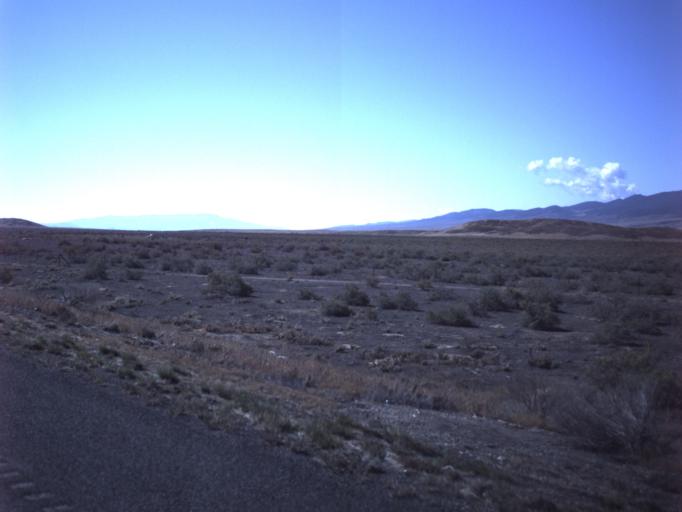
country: US
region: Utah
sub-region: Sanpete County
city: Gunnison
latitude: 39.1869
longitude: -111.8415
